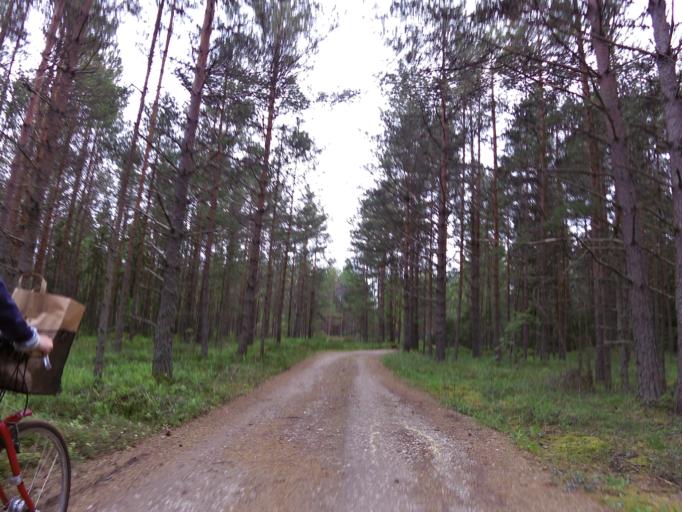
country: EE
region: Harju
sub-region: Paldiski linn
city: Paldiski
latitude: 59.2454
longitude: 23.7474
